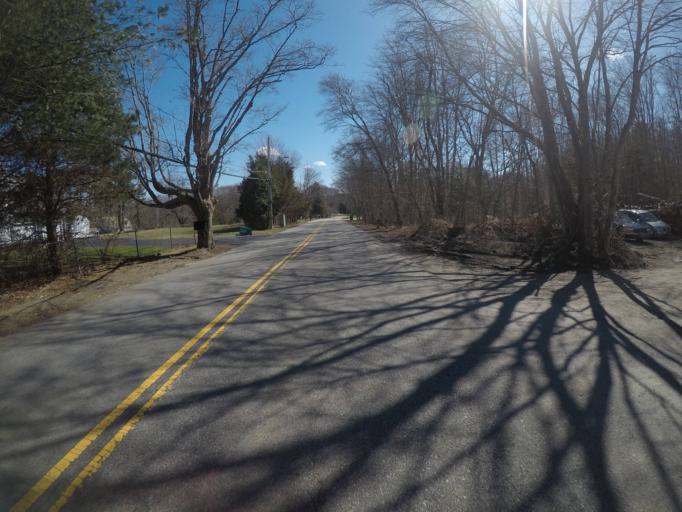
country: US
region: Massachusetts
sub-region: Bristol County
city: Easton
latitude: 42.0085
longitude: -71.0969
